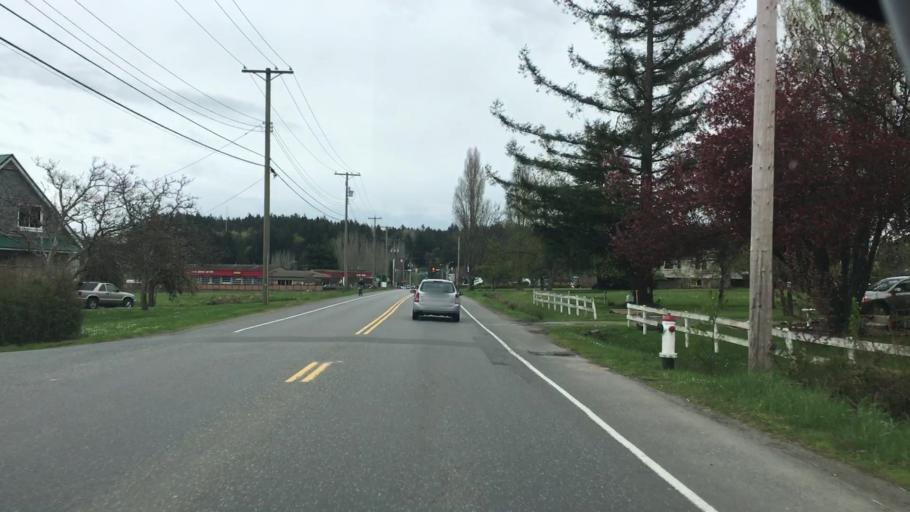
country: CA
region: British Columbia
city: North Saanich
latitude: 48.5676
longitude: -123.4407
